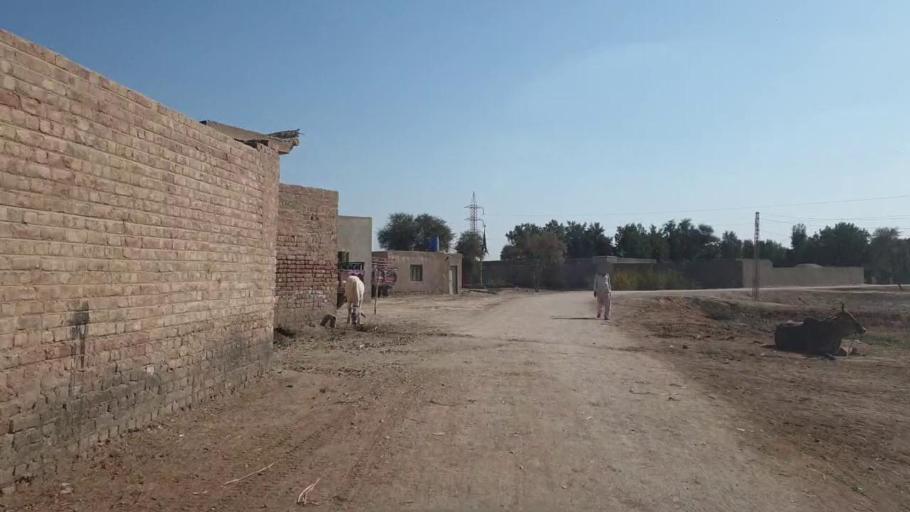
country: PK
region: Sindh
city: Tando Allahyar
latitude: 25.4288
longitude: 68.6941
